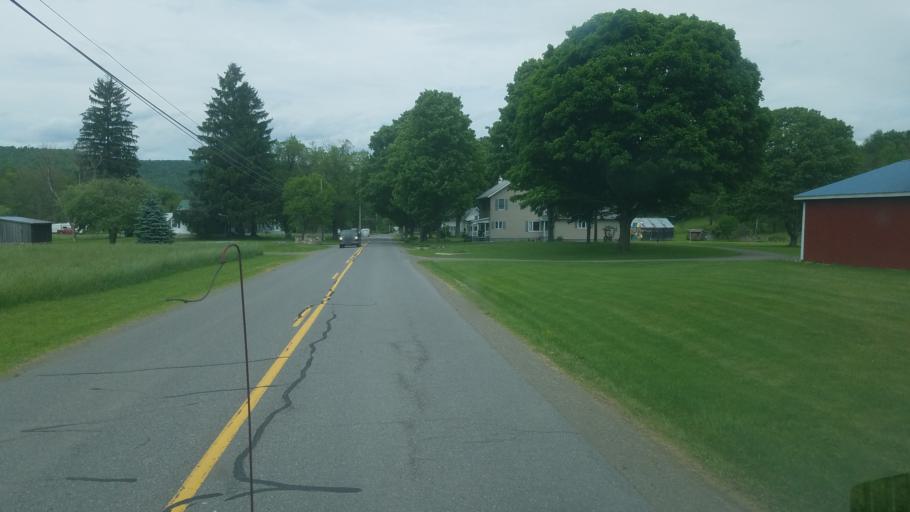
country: US
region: Pennsylvania
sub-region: Tioga County
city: Westfield
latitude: 41.9033
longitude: -77.6050
